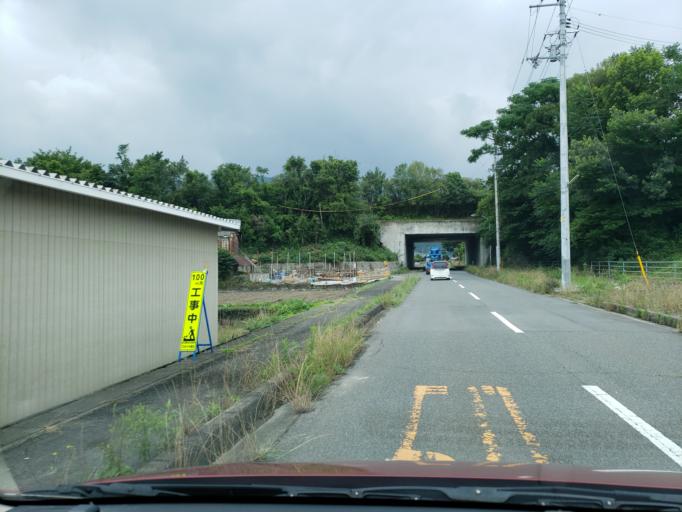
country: JP
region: Tokushima
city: Wakimachi
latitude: 34.0981
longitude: 134.2268
